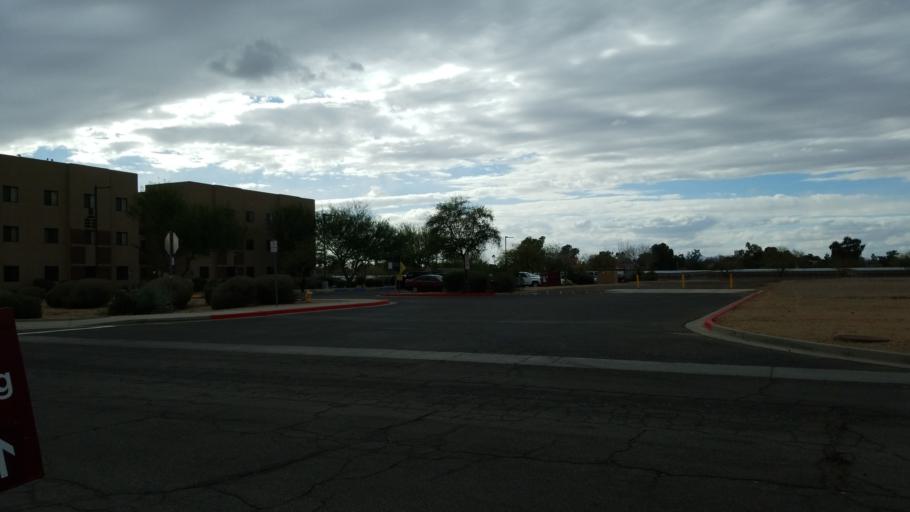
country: US
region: Arizona
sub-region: Maricopa County
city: Glendale
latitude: 33.6095
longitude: -112.1642
